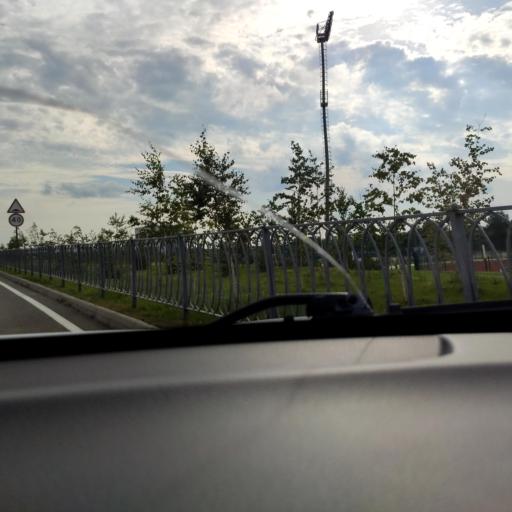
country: RU
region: Tatarstan
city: Sviyazhsk
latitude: 55.7484
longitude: 48.7408
